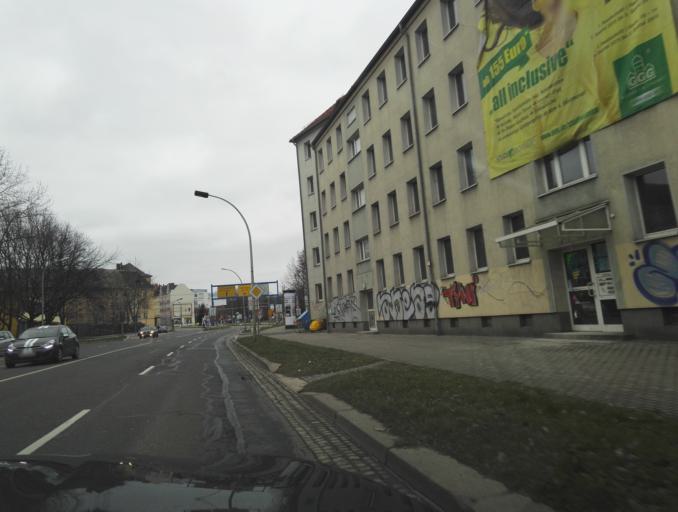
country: DE
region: Saxony
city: Chemnitz
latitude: 50.8253
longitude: 12.9227
